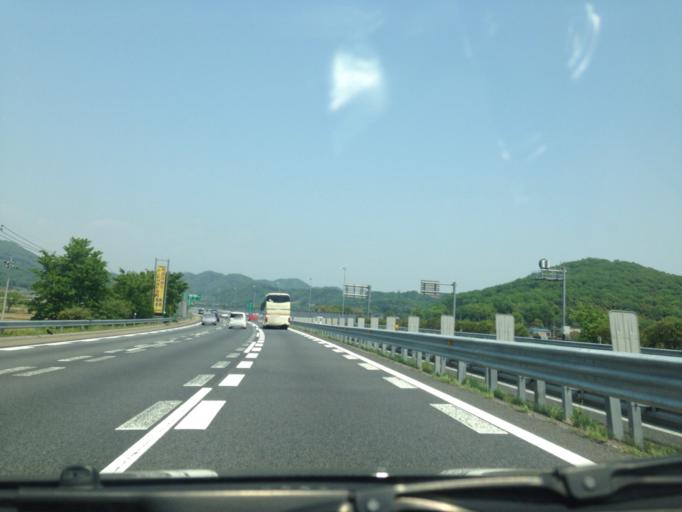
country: JP
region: Tochigi
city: Sano
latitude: 36.3401
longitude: 139.6236
